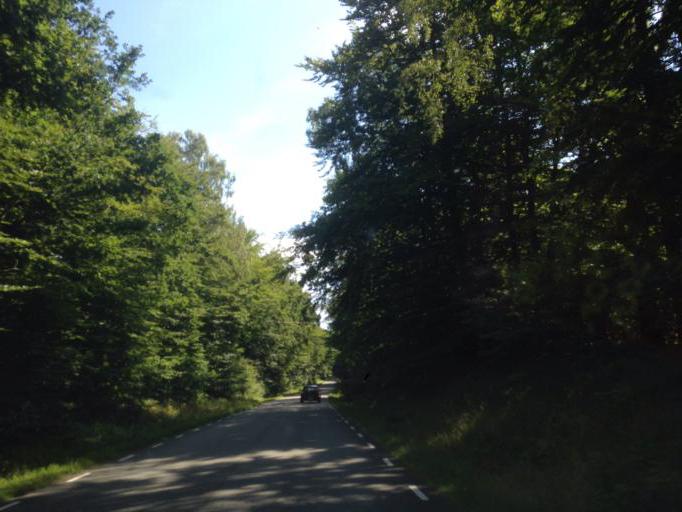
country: SE
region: Skane
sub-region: Simrishamns Kommun
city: Kivik
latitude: 55.6351
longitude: 14.1857
